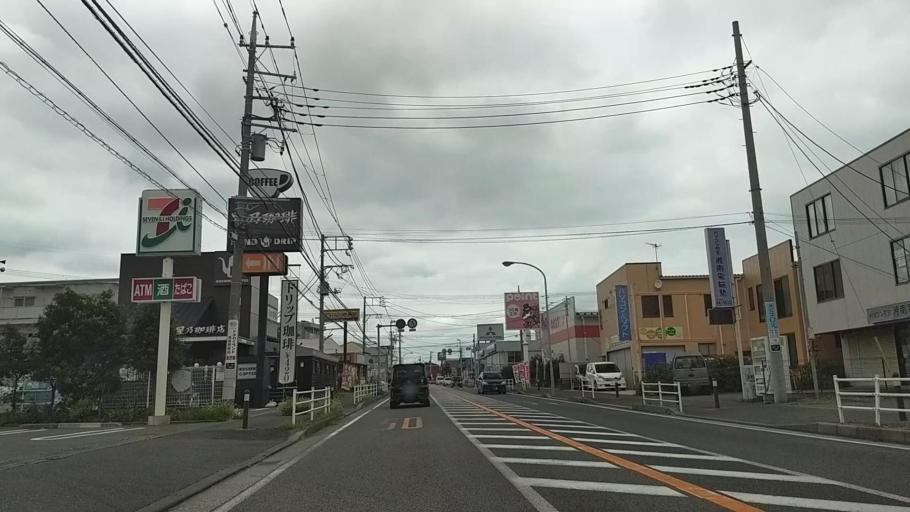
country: JP
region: Kanagawa
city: Minami-rinkan
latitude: 35.4200
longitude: 139.4691
